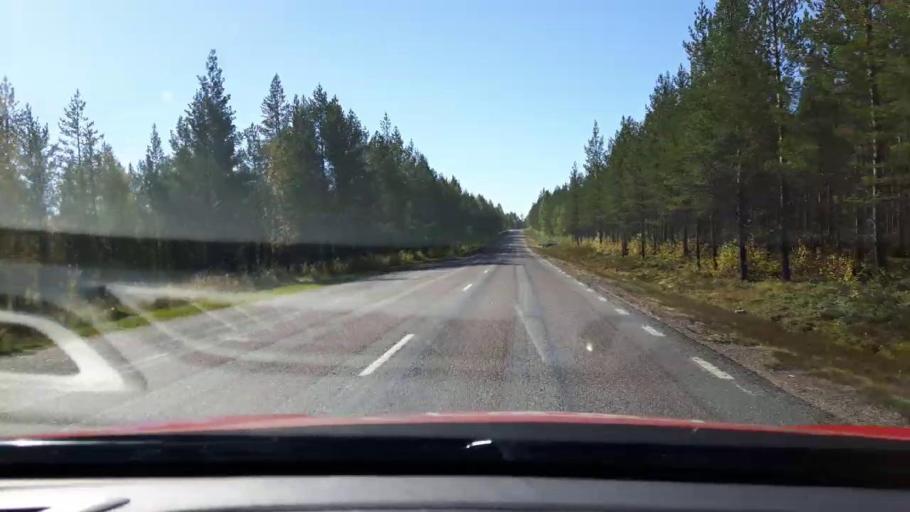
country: SE
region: Jaemtland
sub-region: Harjedalens Kommun
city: Sveg
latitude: 62.1338
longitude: 14.1685
